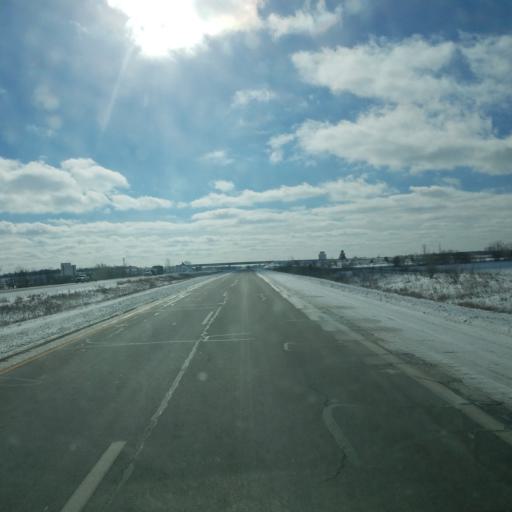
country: US
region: Michigan
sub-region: Clinton County
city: Saint Johns
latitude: 42.9920
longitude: -84.5191
